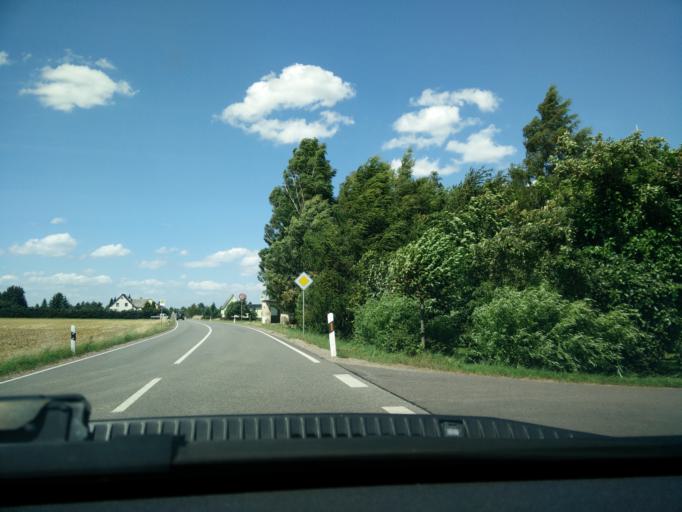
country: DE
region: Saxony
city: Narsdorf
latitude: 51.0250
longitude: 12.7285
